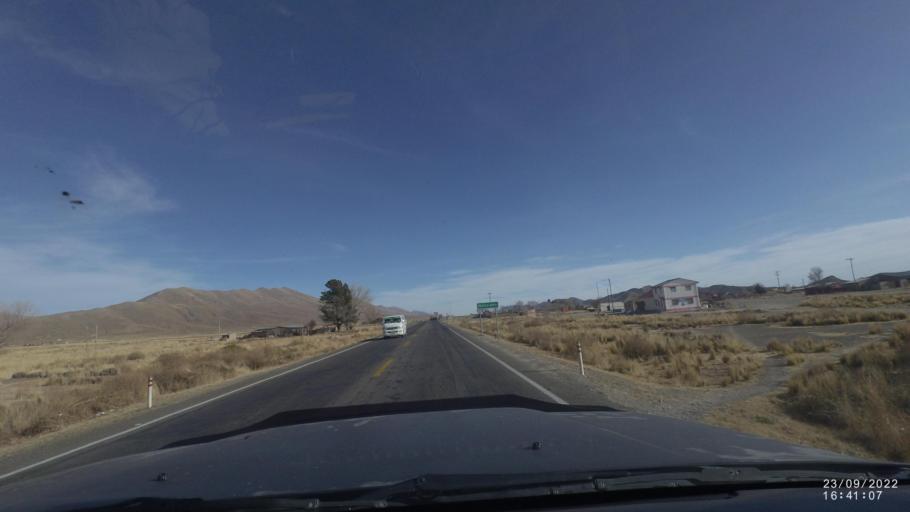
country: BO
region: Oruro
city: Poopo
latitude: -18.2874
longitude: -66.9939
